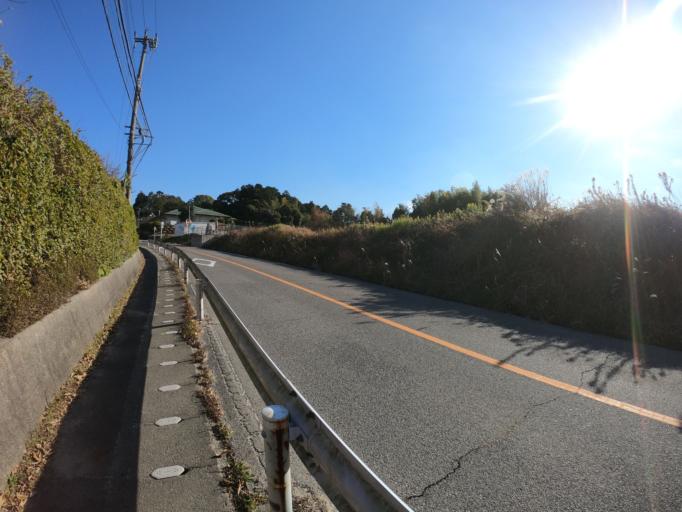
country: JP
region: Aichi
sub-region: Toyota-shi
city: Toyota
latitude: 35.1237
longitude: 137.0442
